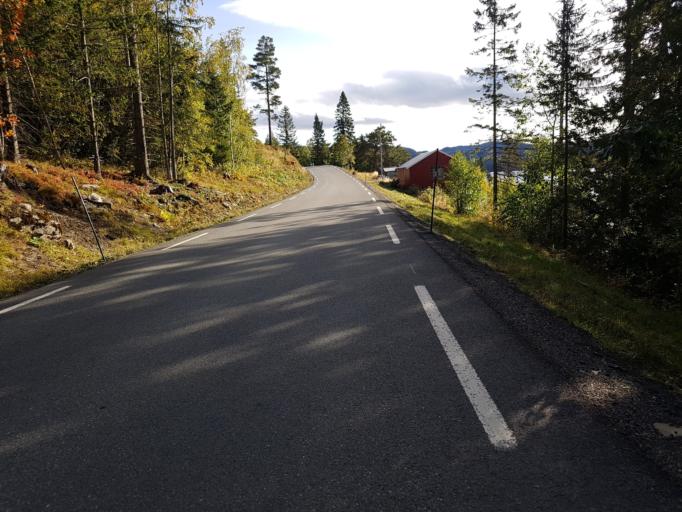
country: NO
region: Sor-Trondelag
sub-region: Malvik
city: Malvik
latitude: 63.3611
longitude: 10.6302
